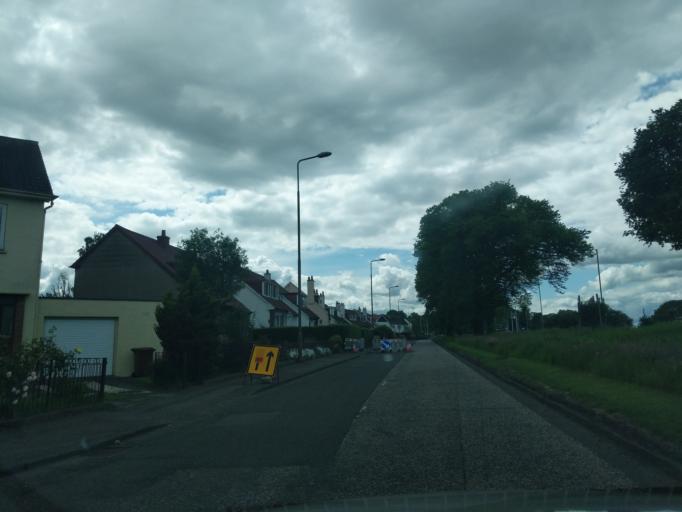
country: GB
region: Scotland
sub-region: Edinburgh
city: Colinton
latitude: 55.9726
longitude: -3.2681
